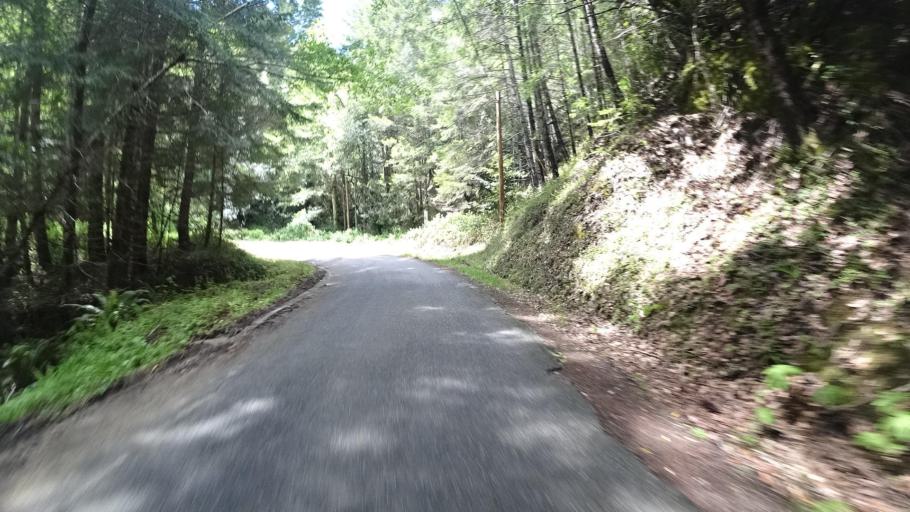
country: US
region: California
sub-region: Humboldt County
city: Blue Lake
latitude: 40.7604
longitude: -123.9135
